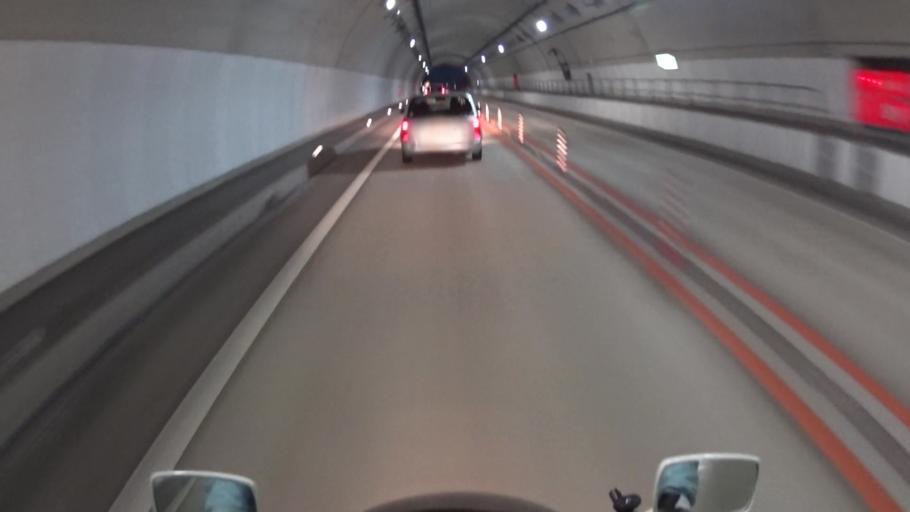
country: JP
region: Kyoto
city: Ayabe
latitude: 35.3037
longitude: 135.3297
